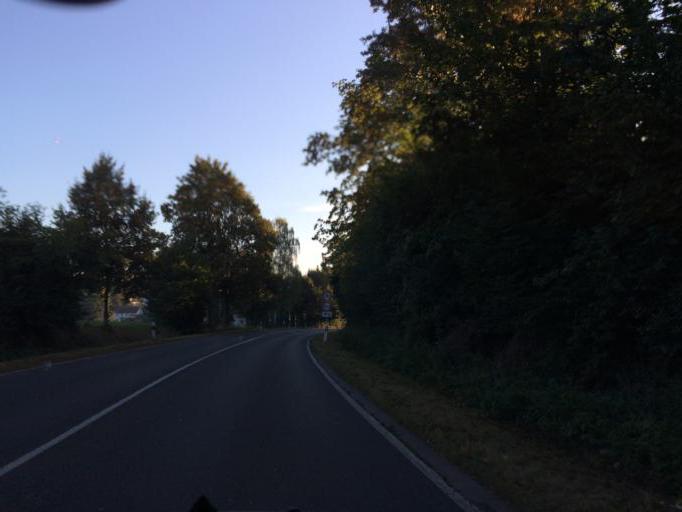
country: DE
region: North Rhine-Westphalia
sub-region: Regierungsbezirk Koln
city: Wachtberg
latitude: 50.6462
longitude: 7.1009
